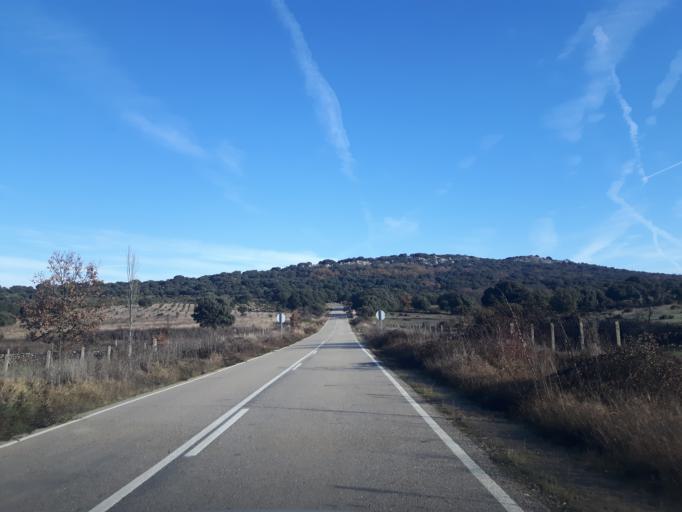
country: ES
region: Castille and Leon
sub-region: Provincia de Salamanca
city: Olmedo de Camaces
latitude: 40.8922
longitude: -6.6216
